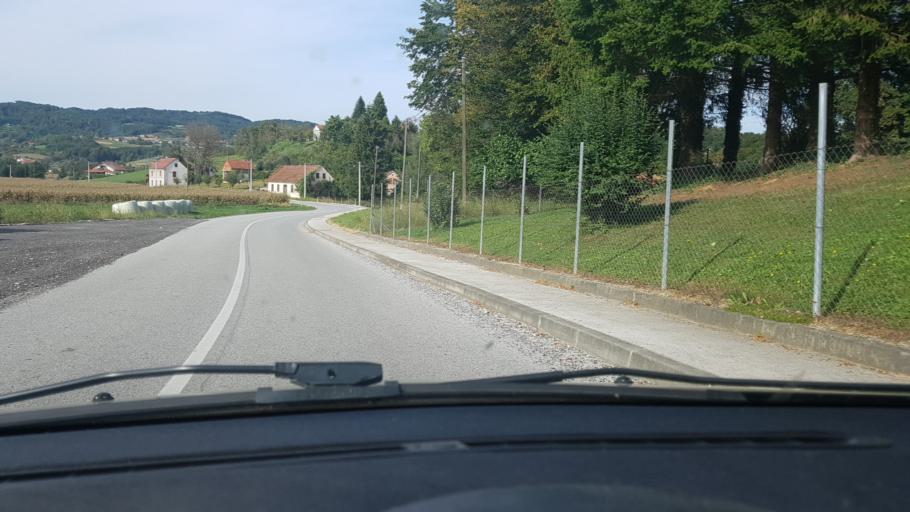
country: HR
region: Krapinsko-Zagorska
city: Mihovljan
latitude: 46.1416
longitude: 15.9639
